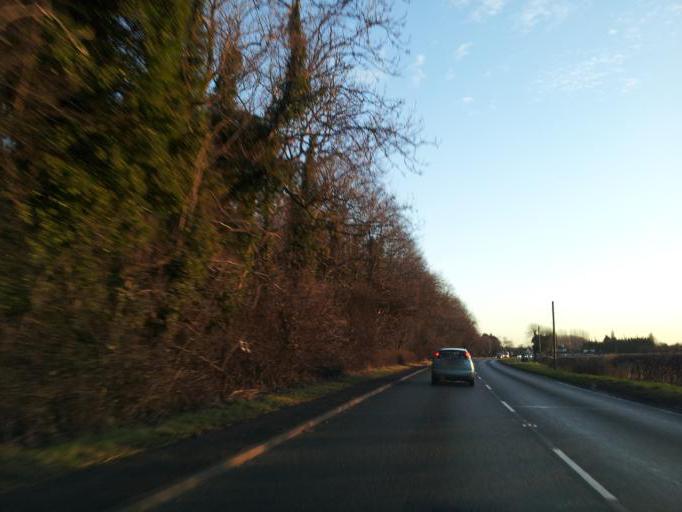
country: GB
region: England
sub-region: Lincolnshire
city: Sudbrooke
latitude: 53.2686
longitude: -0.4307
